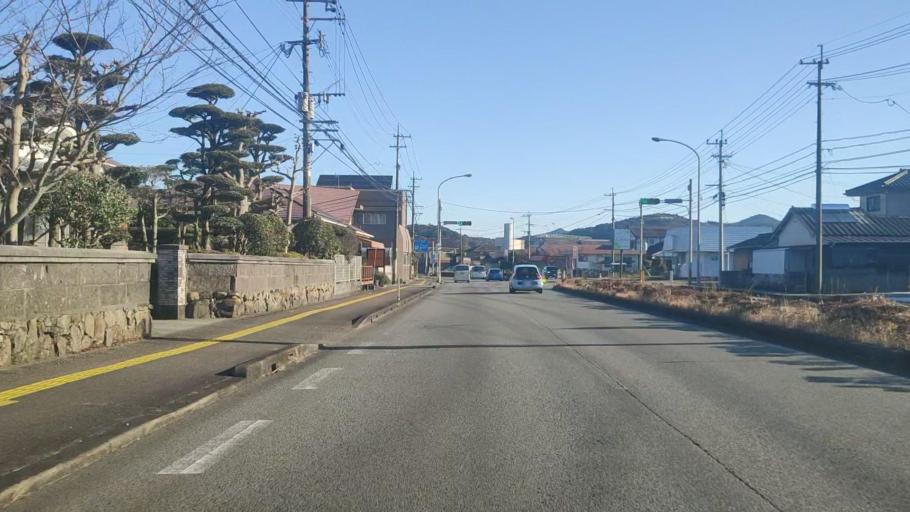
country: JP
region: Miyazaki
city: Nobeoka
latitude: 32.4851
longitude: 131.6619
